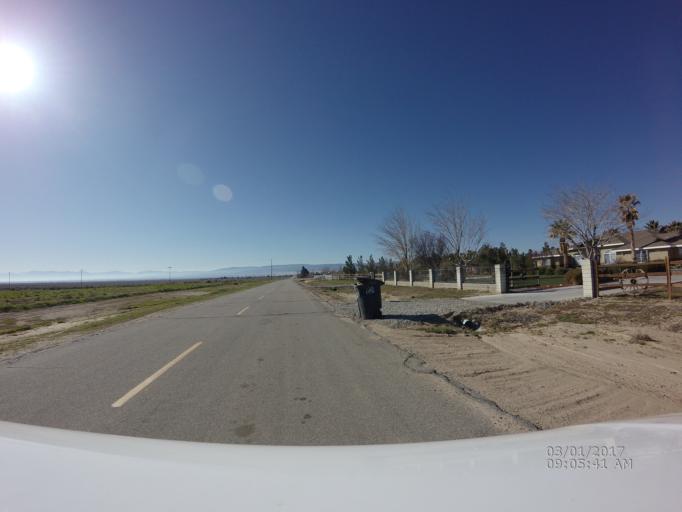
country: US
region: California
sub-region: Los Angeles County
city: Quartz Hill
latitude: 34.7635
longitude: -118.2724
